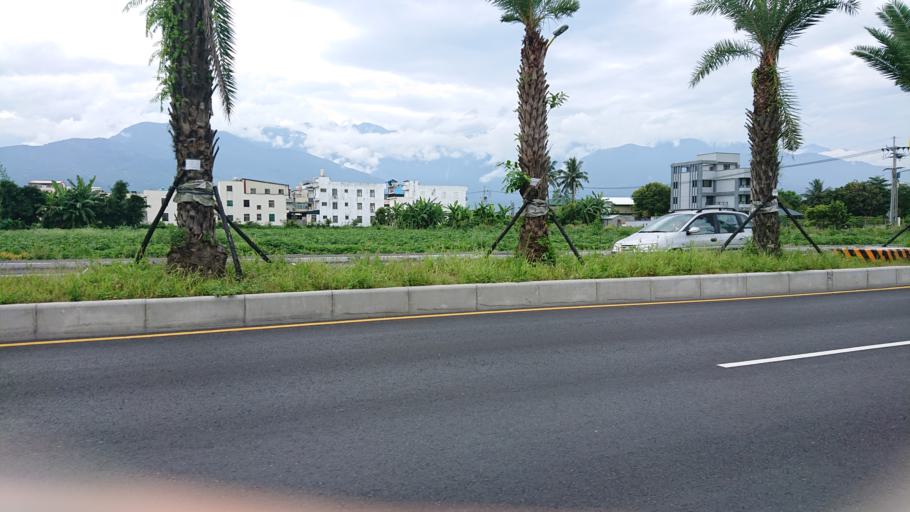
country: TW
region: Taiwan
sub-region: Hualien
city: Hualian
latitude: 23.9507
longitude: 121.5994
